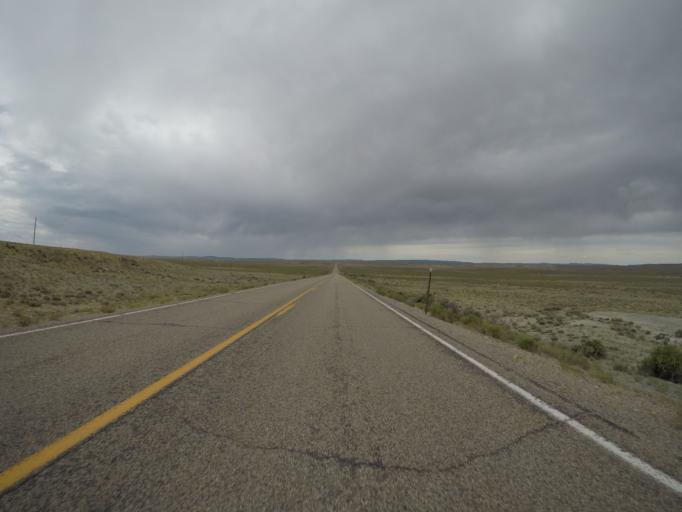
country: US
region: Wyoming
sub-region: Lincoln County
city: Kemmerer
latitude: 41.9633
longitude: -110.1350
